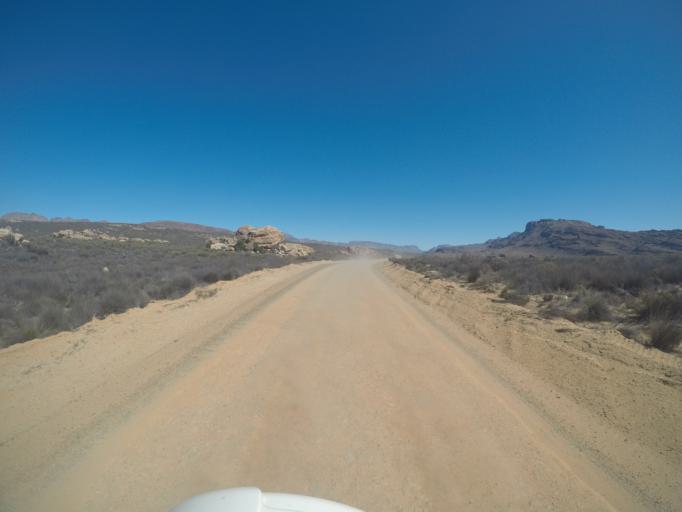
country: ZA
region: Western Cape
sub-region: West Coast District Municipality
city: Clanwilliam
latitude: -32.5095
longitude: 19.3111
